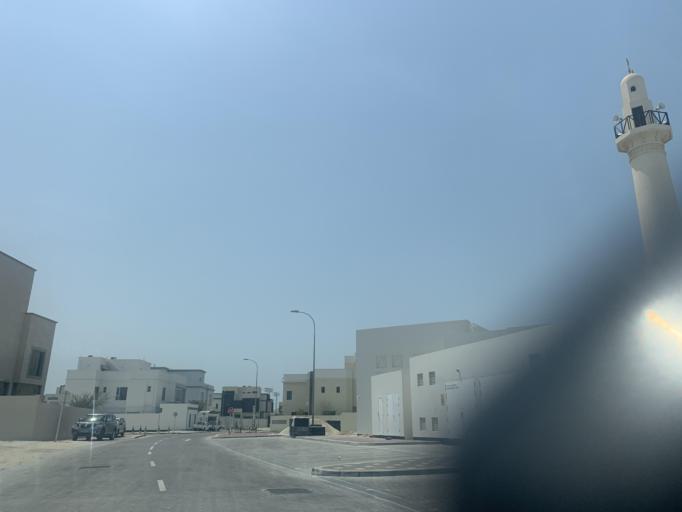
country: BH
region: Muharraq
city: Al Muharraq
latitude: 26.2978
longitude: 50.6395
